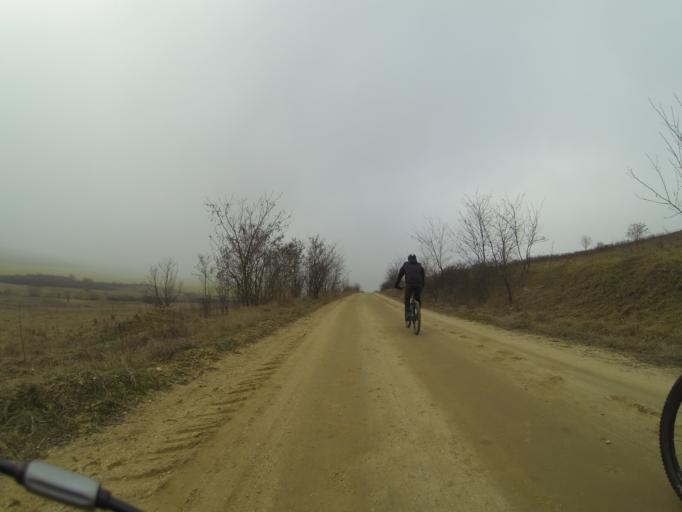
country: RO
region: Mehedinti
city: Padina Mica
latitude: 44.4810
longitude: 23.0389
